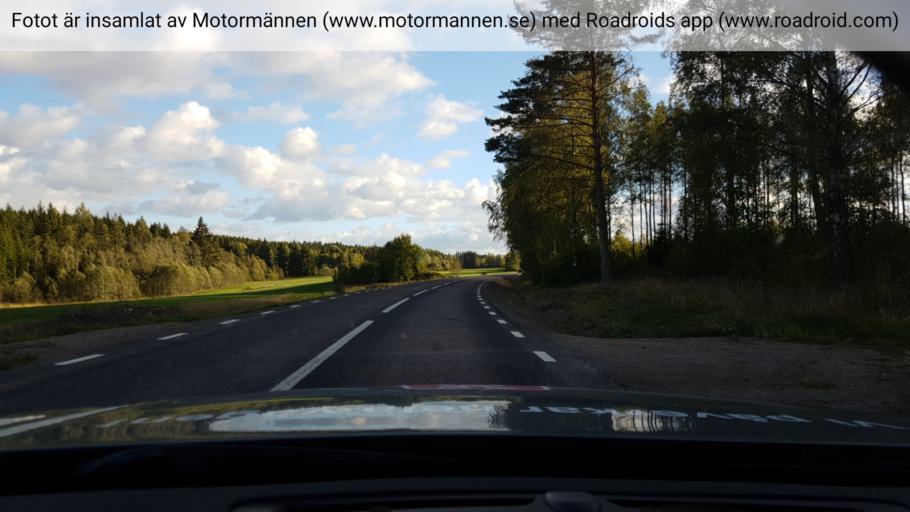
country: SE
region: Vaermland
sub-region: Karlstads Kommun
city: Molkom
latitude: 59.7094
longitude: 13.6798
